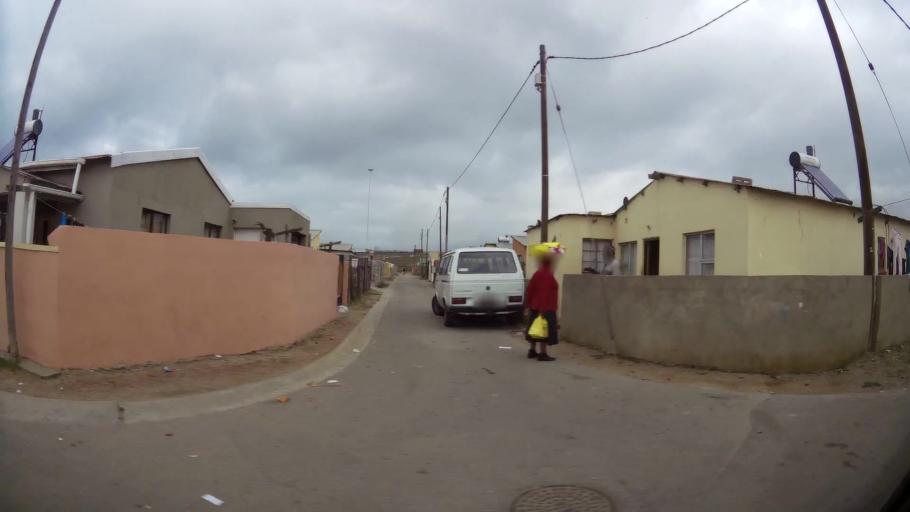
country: ZA
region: Eastern Cape
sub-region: Nelson Mandela Bay Metropolitan Municipality
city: Port Elizabeth
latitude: -33.8885
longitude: 25.6012
